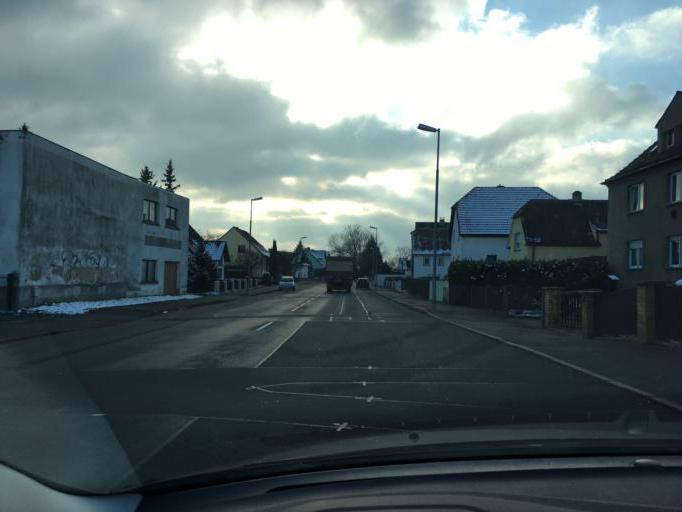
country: DE
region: Saxony
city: Brandis
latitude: 51.3557
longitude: 12.5798
